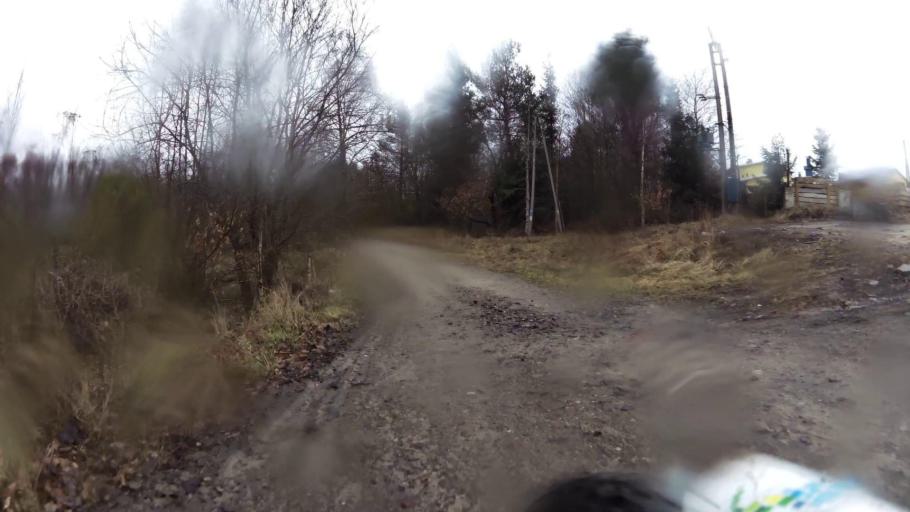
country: PL
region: Pomeranian Voivodeship
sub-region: Powiat bytowski
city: Miastko
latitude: 54.0423
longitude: 17.0423
